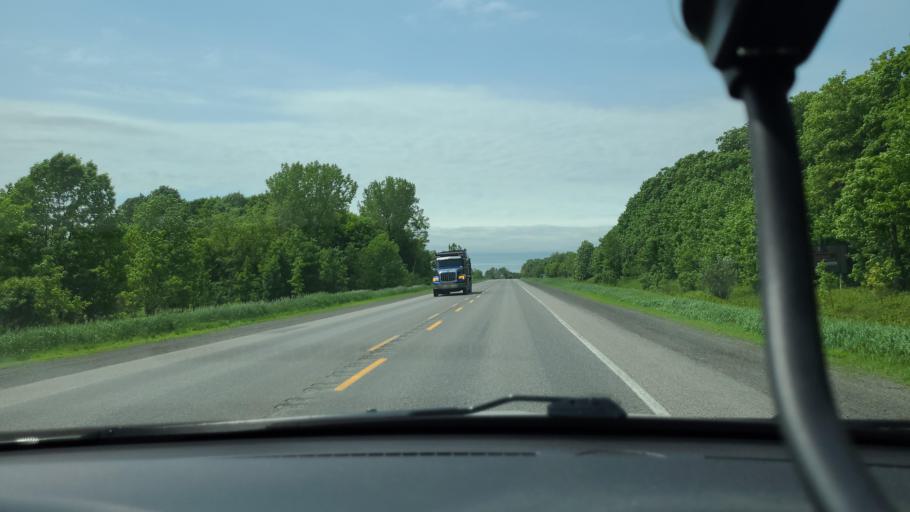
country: CA
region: Quebec
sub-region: Lanaudiere
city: Saint-Jacques
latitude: 45.9679
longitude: -73.5557
